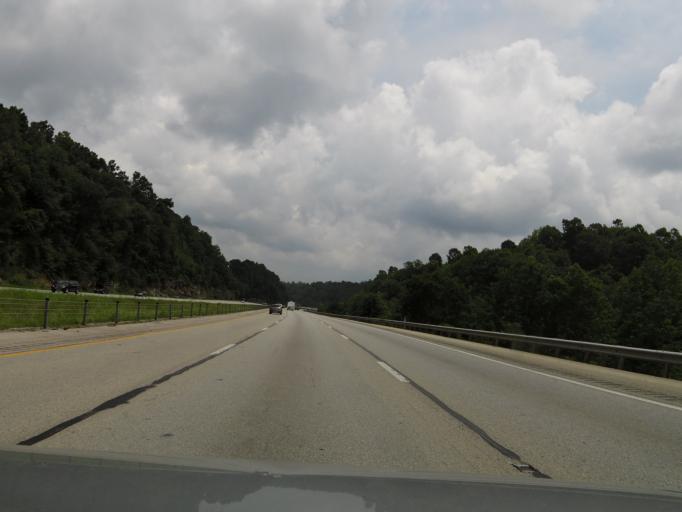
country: US
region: Kentucky
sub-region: Hardin County
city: Elizabethtown
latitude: 37.7380
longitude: -85.8023
